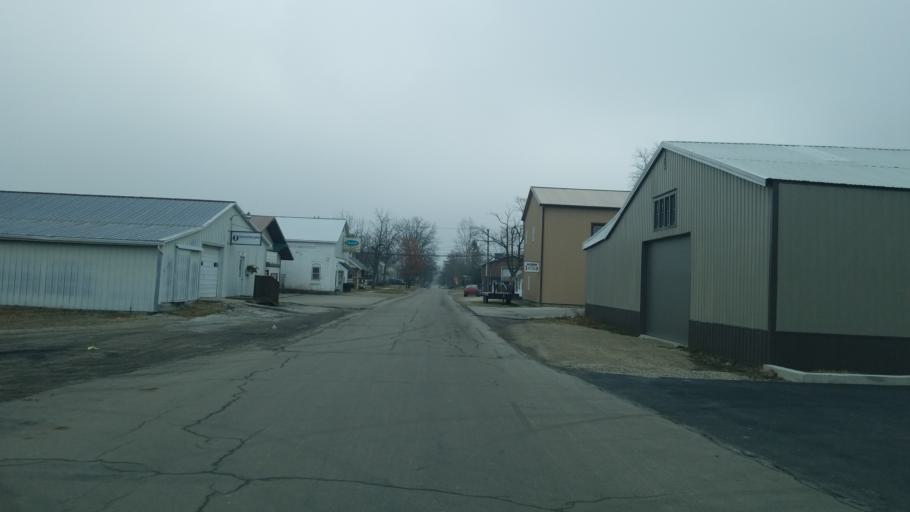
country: US
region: Indiana
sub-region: Adams County
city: Berne
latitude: 40.6589
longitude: -84.9489
